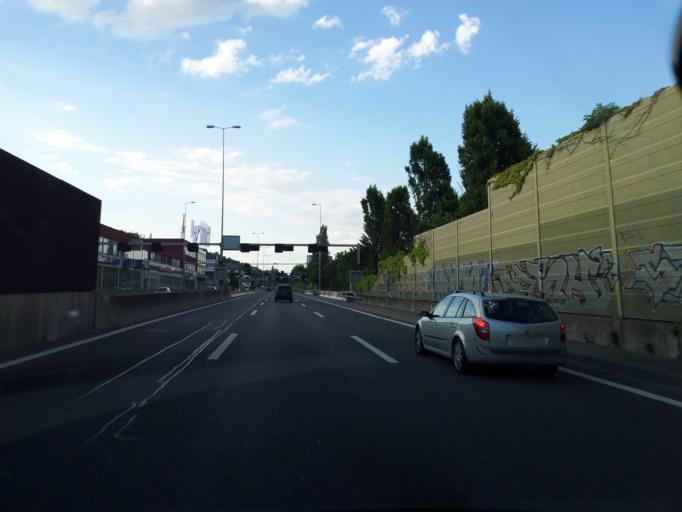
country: CH
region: Lucerne
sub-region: Lucerne-Land District
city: Horw
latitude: 47.0287
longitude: 8.2944
